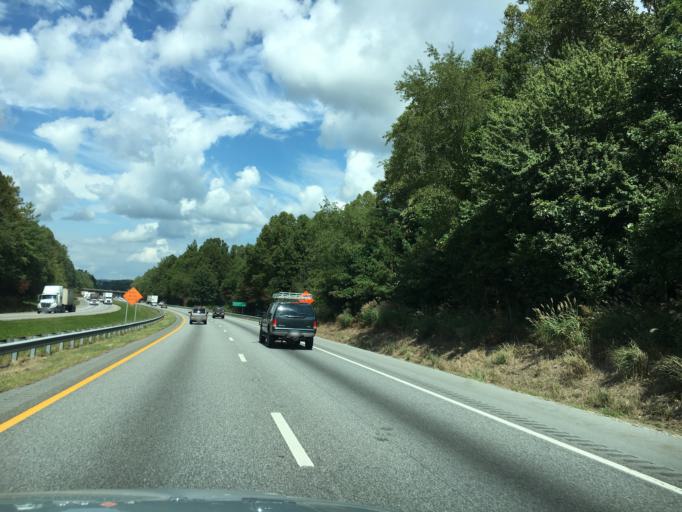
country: US
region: North Carolina
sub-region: Henderson County
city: Barker Heights
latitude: 35.3107
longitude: -82.4174
